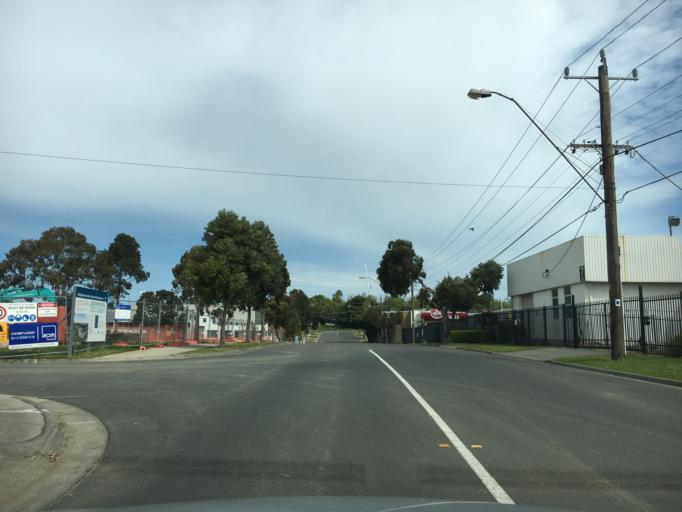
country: AU
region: Victoria
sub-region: Monash
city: Chadstone
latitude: -37.8927
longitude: 145.0963
